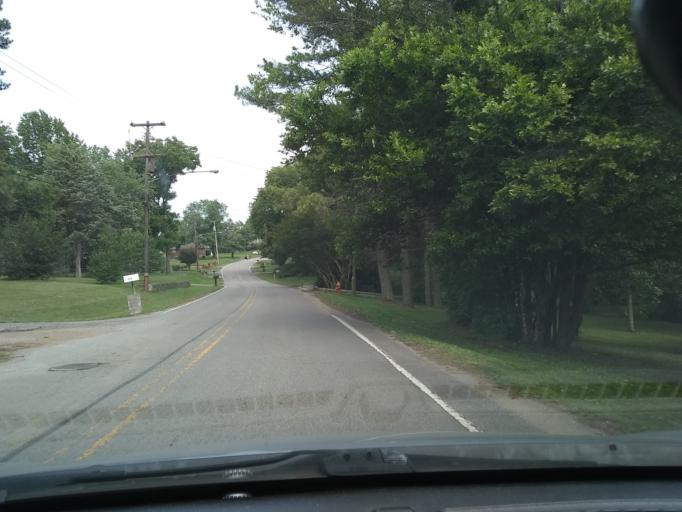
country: US
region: Tennessee
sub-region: Davidson County
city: Oak Hill
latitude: 36.1183
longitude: -86.7089
